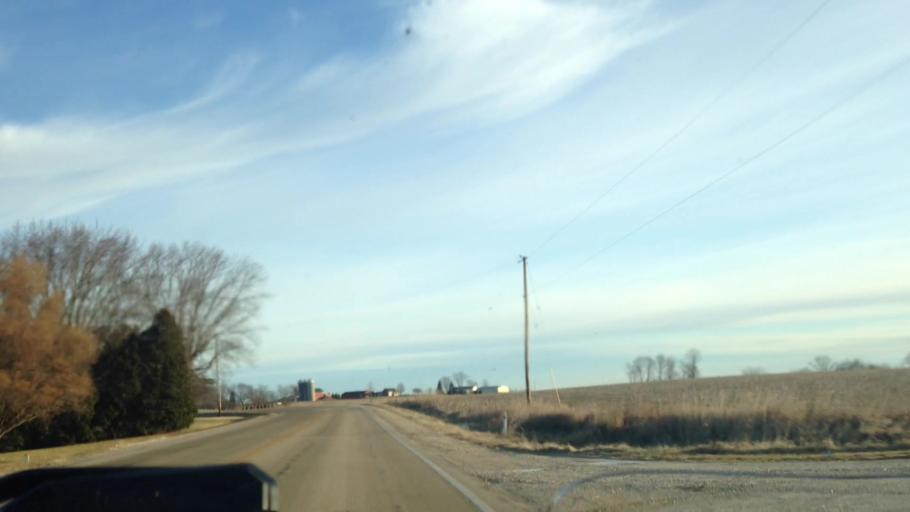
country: US
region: Wisconsin
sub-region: Dodge County
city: Theresa
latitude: 43.5314
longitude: -88.4991
